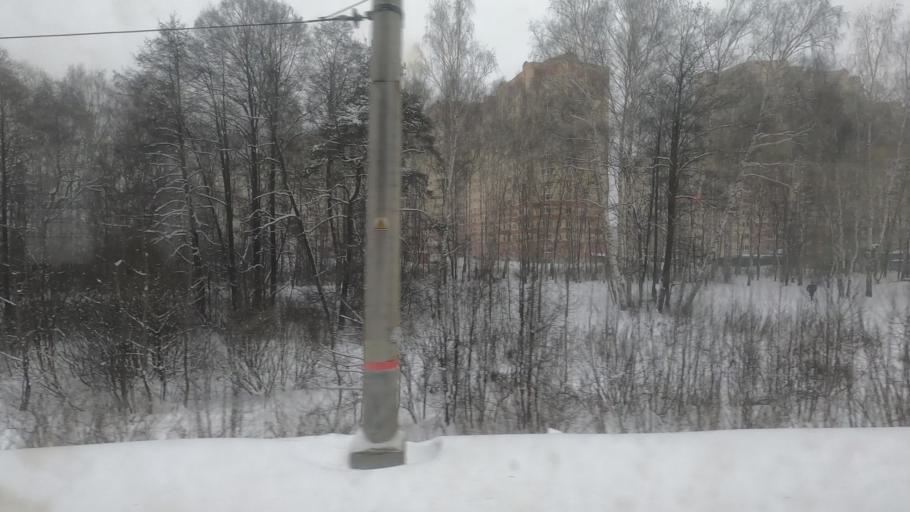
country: RU
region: Moskovskaya
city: Chornaya
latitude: 55.7532
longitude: 38.0574
